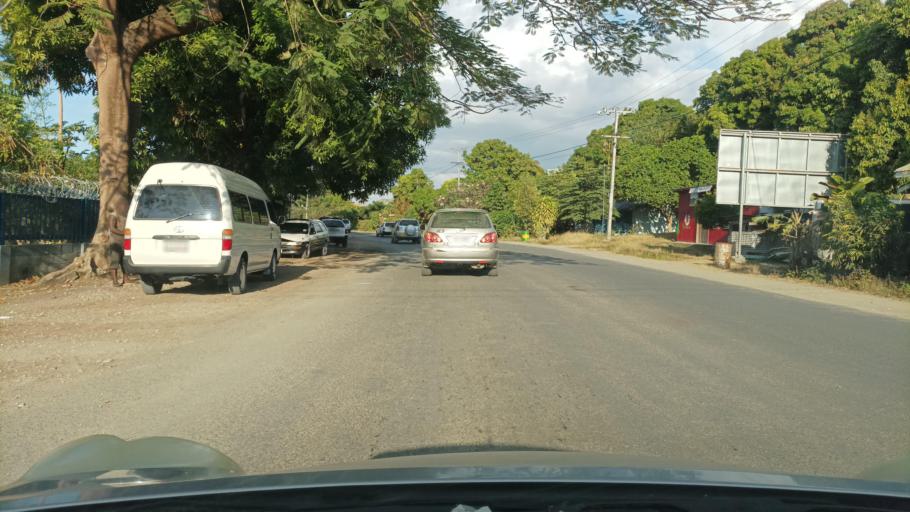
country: SB
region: Guadalcanal
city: Honiara
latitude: -9.4284
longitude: 159.9376
